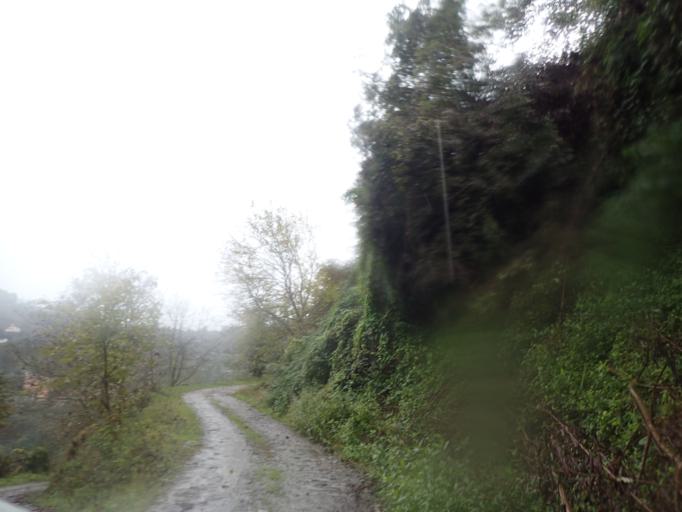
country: TR
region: Ordu
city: Persembe
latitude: 41.0354
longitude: 37.7325
